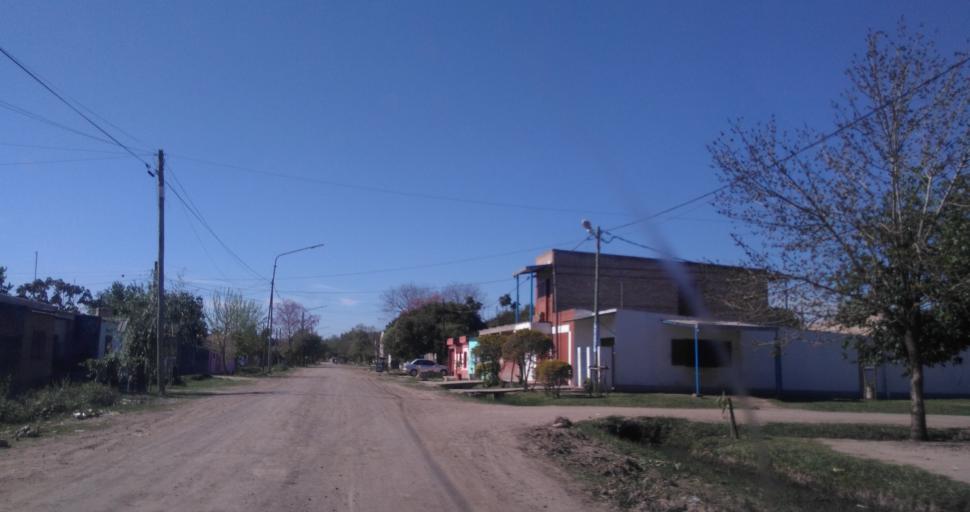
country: AR
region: Chaco
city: Fontana
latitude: -27.4240
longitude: -59.0266
